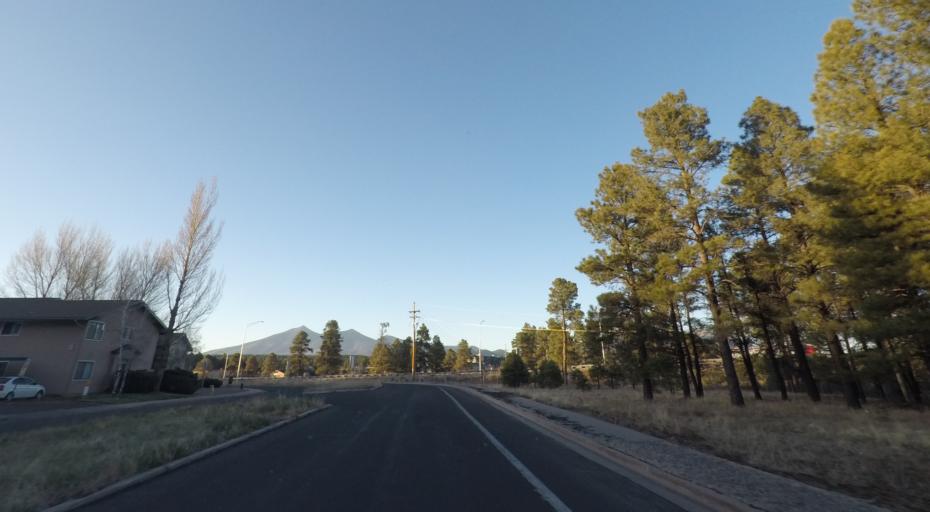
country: US
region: Arizona
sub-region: Coconino County
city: Flagstaff
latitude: 35.1721
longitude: -111.6676
